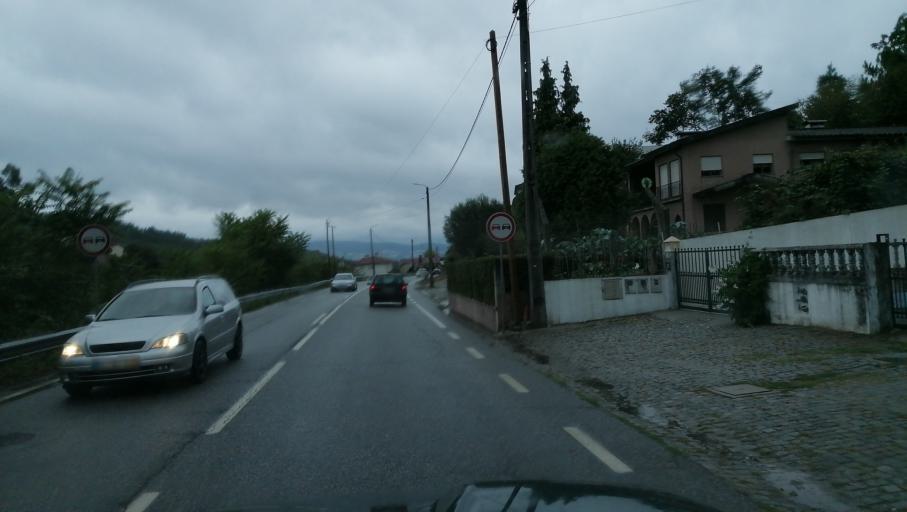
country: PT
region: Braga
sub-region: Guimaraes
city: Moreira de Conegos
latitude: 41.3967
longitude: -8.3260
